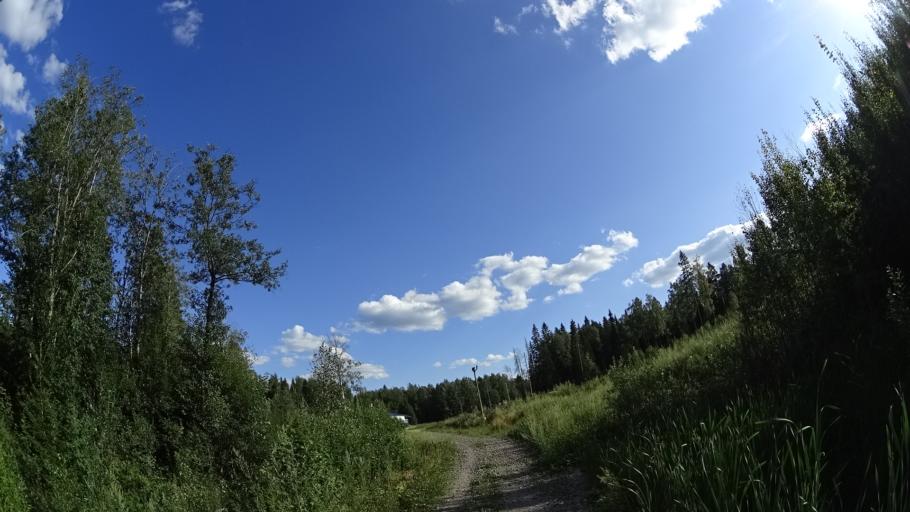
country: FI
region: Uusimaa
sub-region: Helsinki
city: Vihti
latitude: 60.3749
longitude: 24.3717
